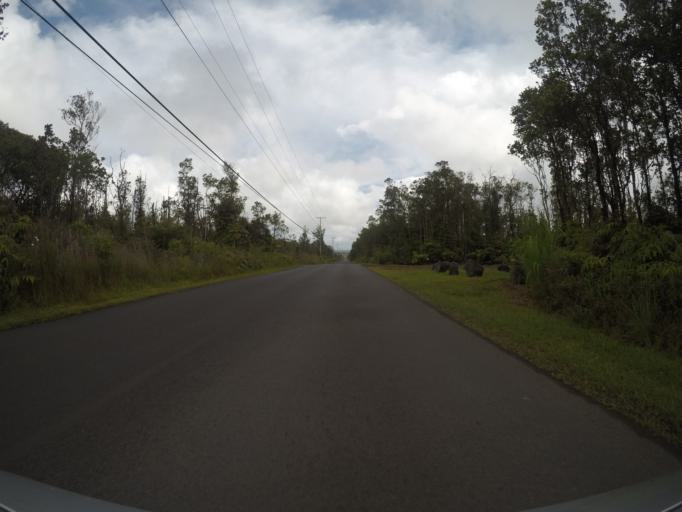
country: US
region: Hawaii
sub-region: Hawaii County
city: Fern Acres
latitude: 19.4701
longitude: -155.1371
